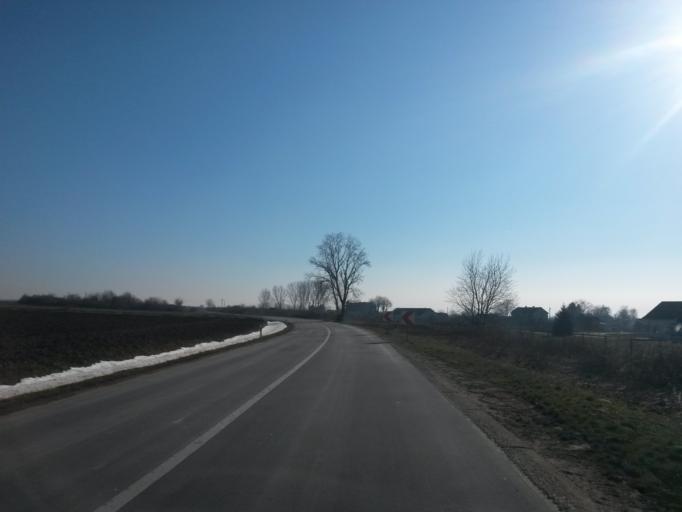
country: HR
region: Osjecko-Baranjska
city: Dalj
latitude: 45.5014
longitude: 18.9612
